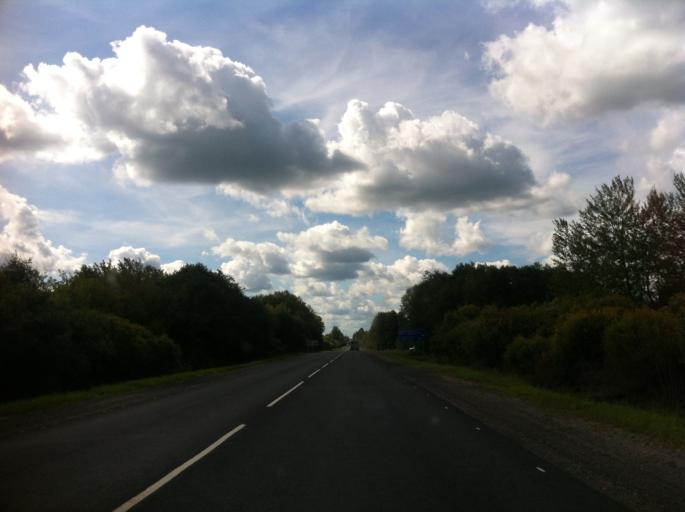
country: RU
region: Pskov
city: Izborsk
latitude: 57.7280
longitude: 27.9629
